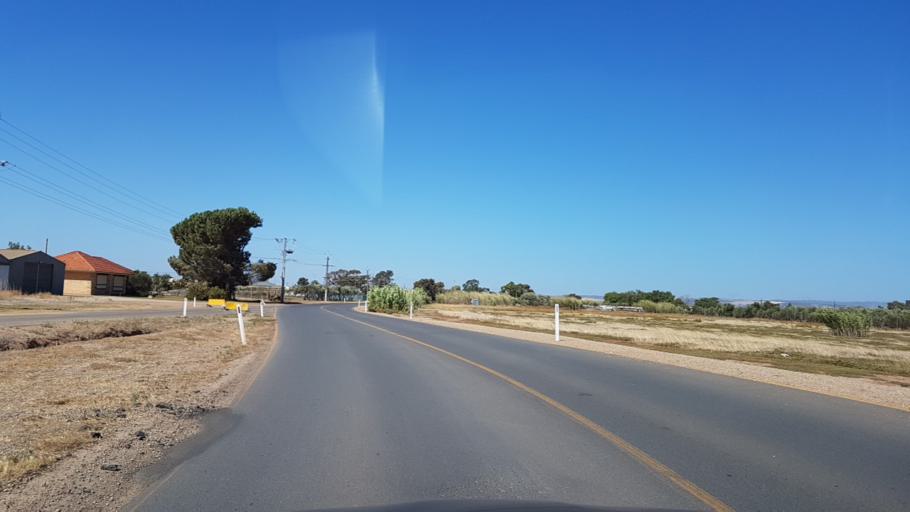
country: AU
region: South Australia
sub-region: Playford
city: Virginia
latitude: -34.7259
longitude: 138.5756
